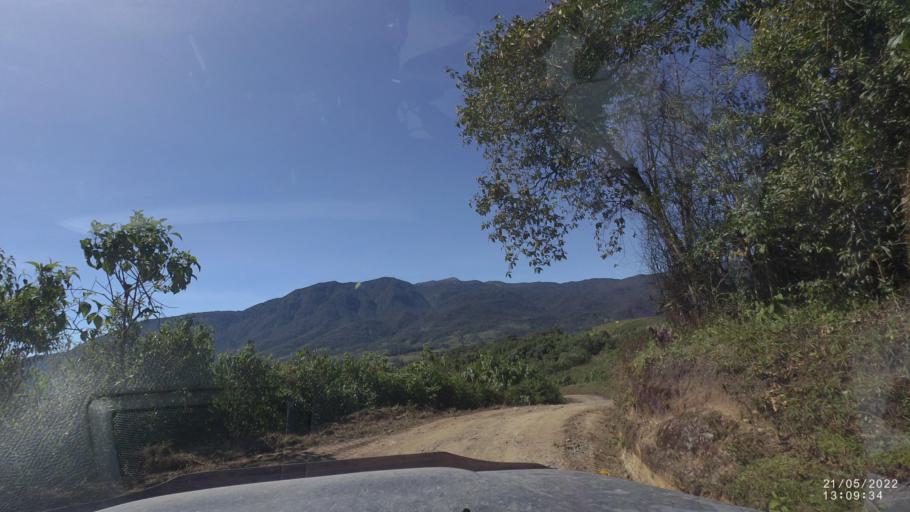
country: BO
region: Cochabamba
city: Colomi
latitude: -17.1434
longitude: -65.9430
